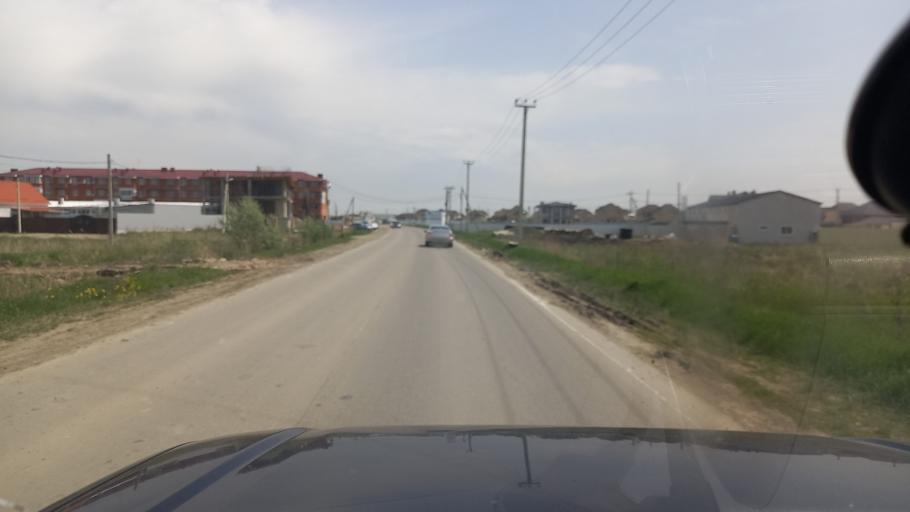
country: RU
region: Adygeya
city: Yablonovskiy
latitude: 44.9852
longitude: 38.9718
